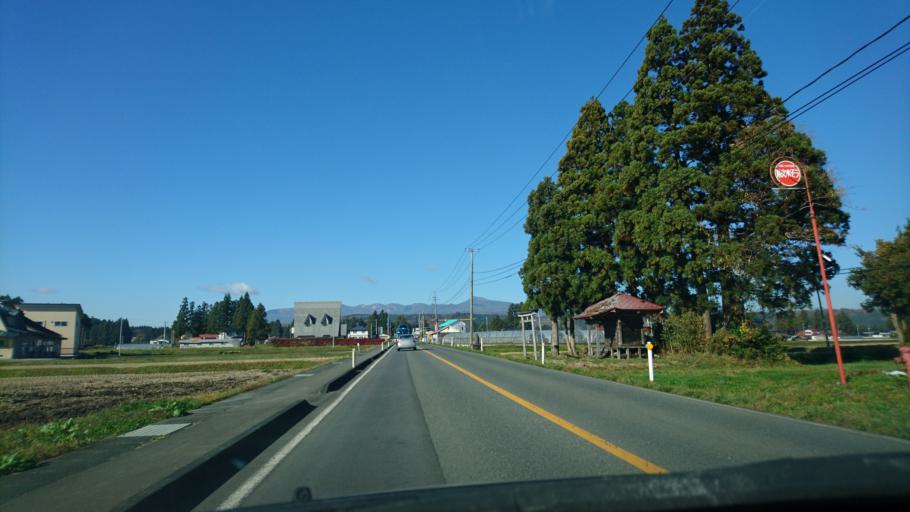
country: JP
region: Iwate
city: Mizusawa
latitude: 39.1299
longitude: 141.0479
